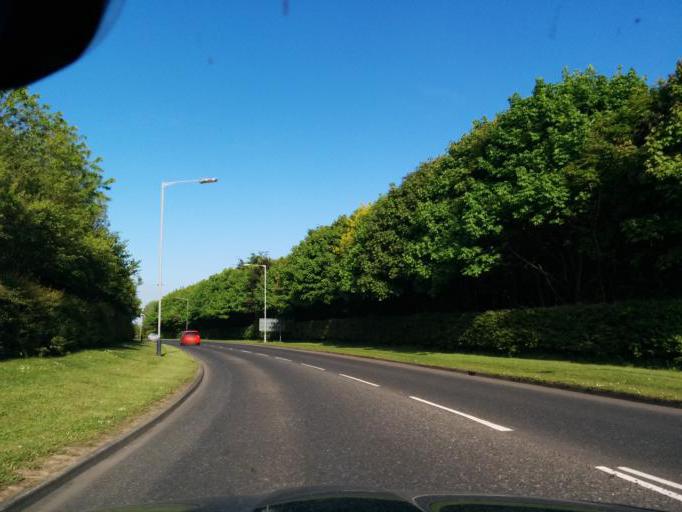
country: GB
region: England
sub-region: Northumberland
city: Cramlington
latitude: 55.0954
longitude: -1.5895
